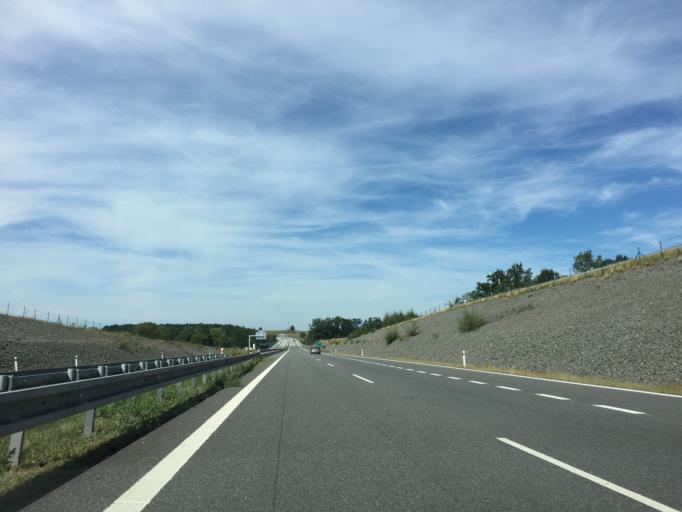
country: CZ
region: Jihocesky
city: Sobeslav
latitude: 49.2691
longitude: 14.7366
